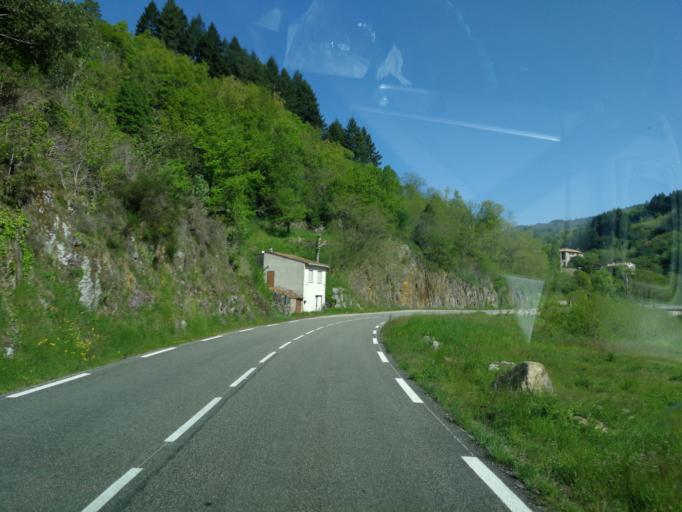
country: FR
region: Rhone-Alpes
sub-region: Departement de l'Ardeche
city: Saint-Sauveur-de-Montagut
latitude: 44.8382
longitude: 4.5736
